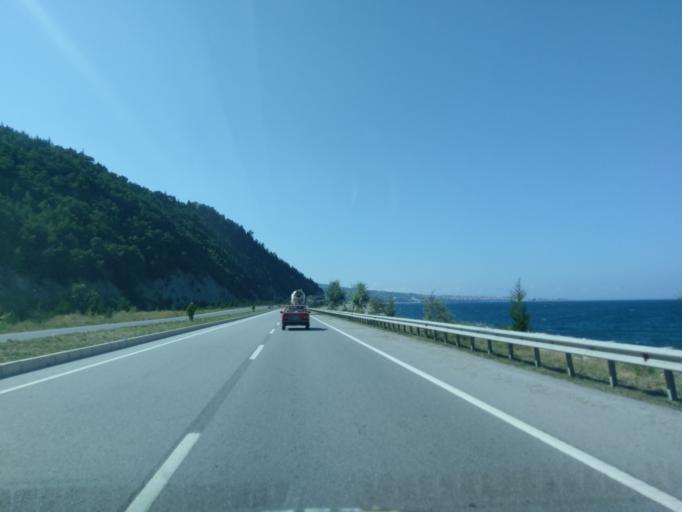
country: TR
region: Sinop
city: Gerze
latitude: 41.7463
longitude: 35.2458
